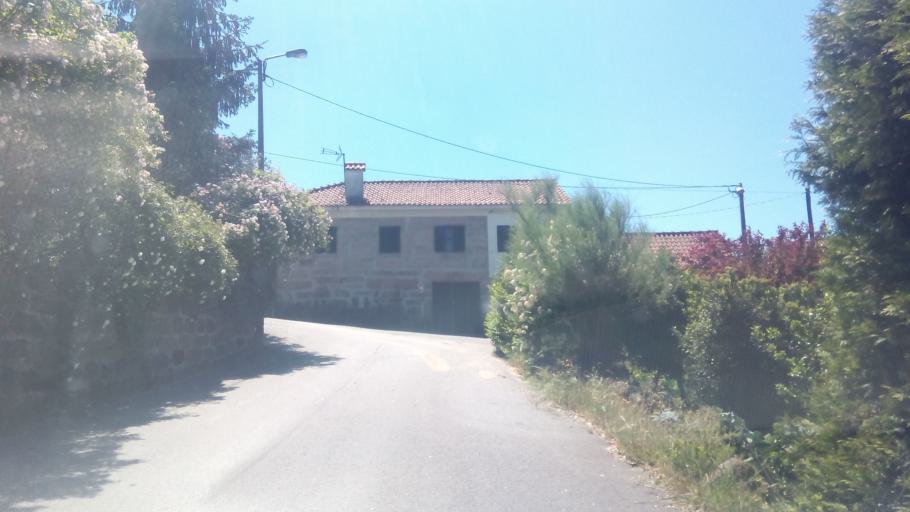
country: PT
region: Porto
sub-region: Paredes
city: Casteloes de Cepeda
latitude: 41.1965
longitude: -8.3478
